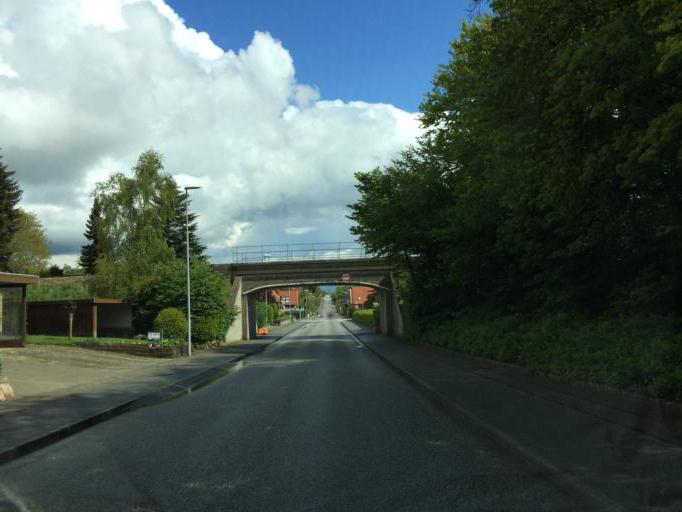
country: DK
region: Central Jutland
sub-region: Holstebro Kommune
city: Holstebro
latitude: 56.3544
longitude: 8.6070
